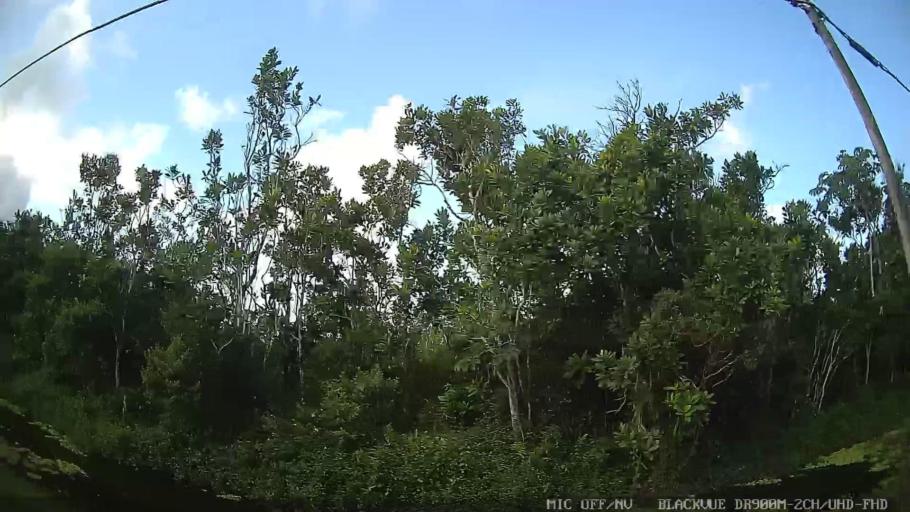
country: BR
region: Sao Paulo
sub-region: Itanhaem
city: Itanhaem
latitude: -24.1646
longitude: -46.8406
